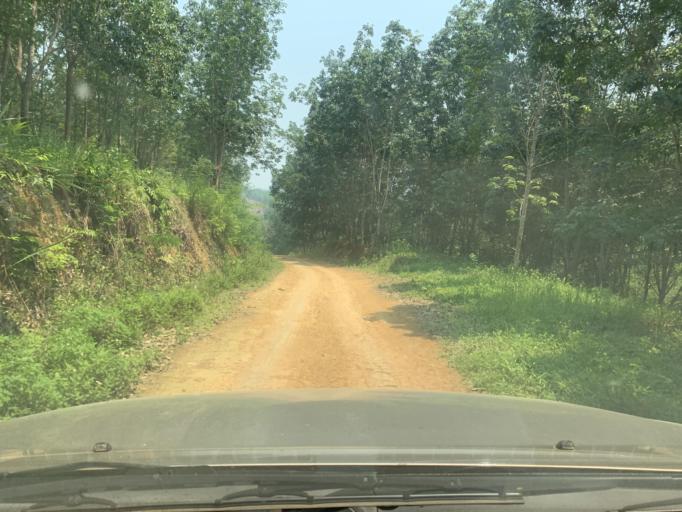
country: LA
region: Louangphabang
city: Xiang Ngeun
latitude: 19.8315
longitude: 102.2235
